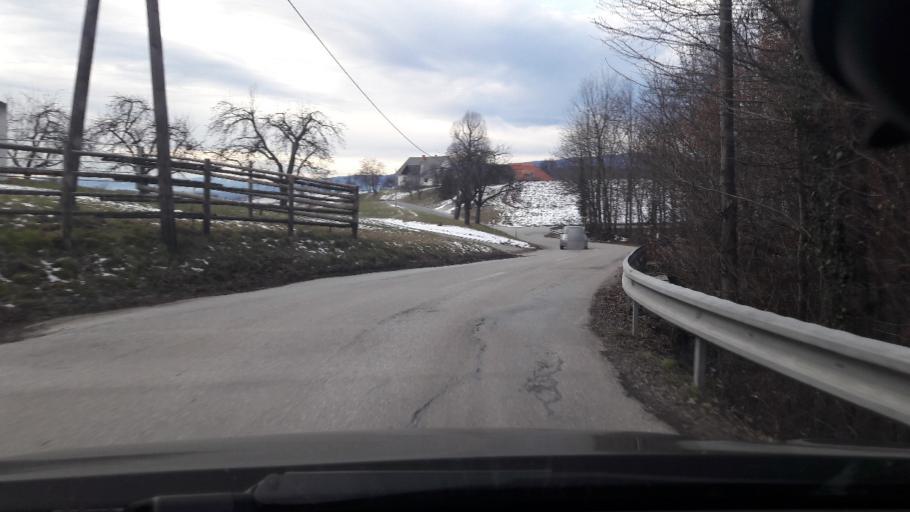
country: AT
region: Styria
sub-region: Politischer Bezirk Graz-Umgebung
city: Sankt Oswald bei Plankenwarth
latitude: 47.0831
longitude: 15.2757
